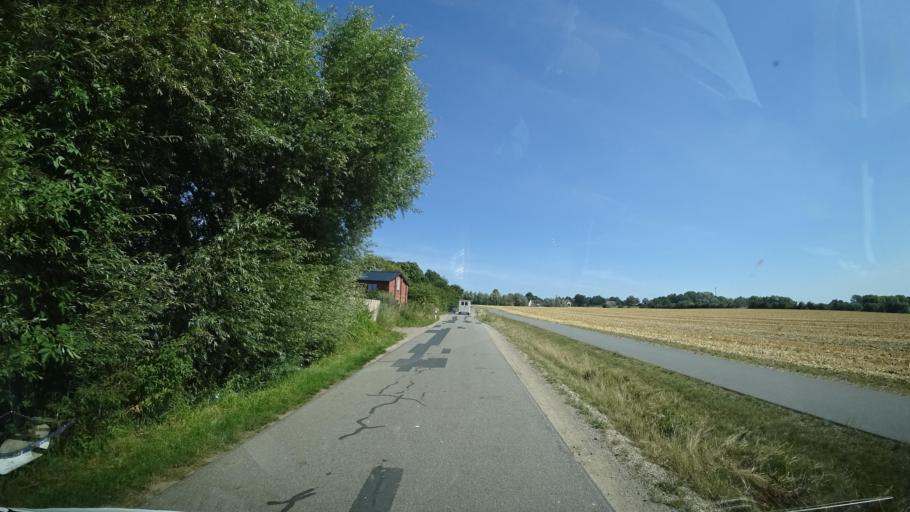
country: DE
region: Mecklenburg-Vorpommern
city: Blowatz
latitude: 54.0219
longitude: 11.5550
